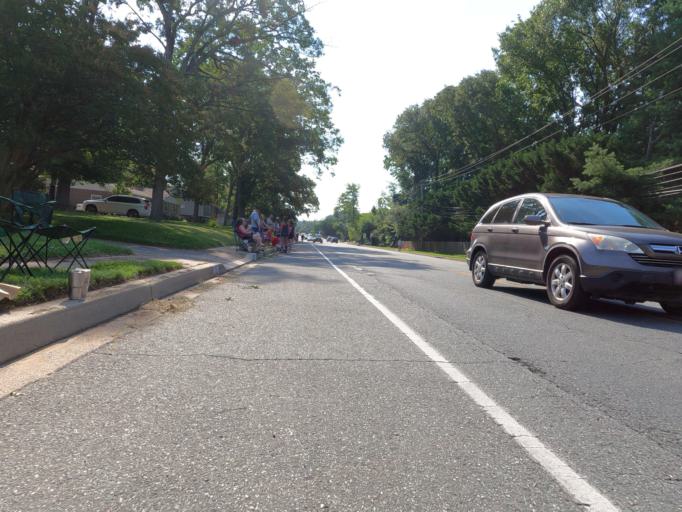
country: US
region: Maryland
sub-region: Anne Arundel County
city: Arden on the Severn
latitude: 39.0771
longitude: -76.5661
